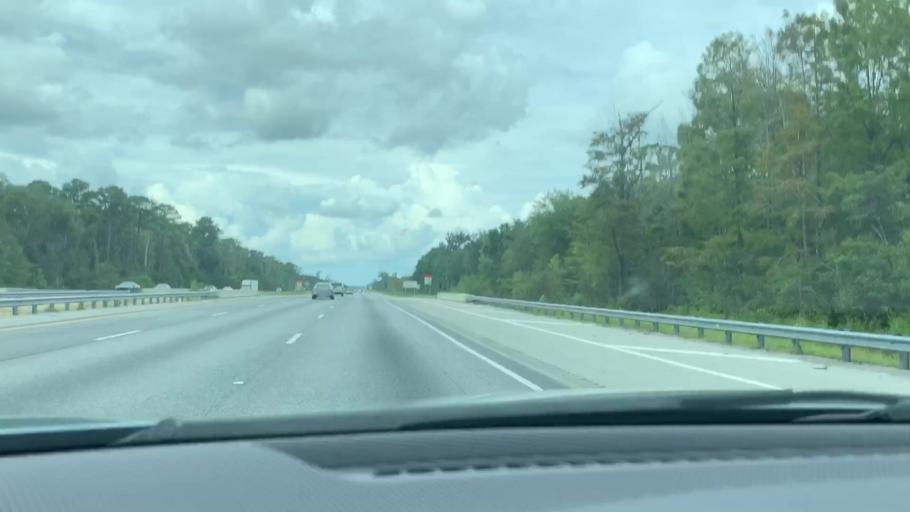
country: US
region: Georgia
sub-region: McIntosh County
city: Darien
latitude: 31.4408
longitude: -81.4443
